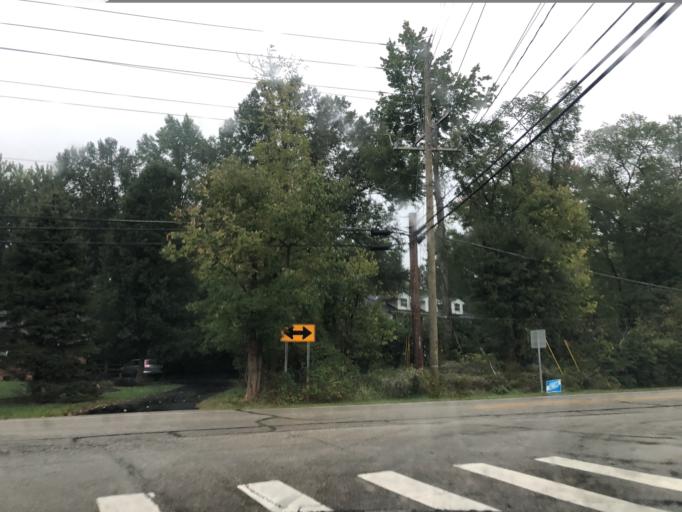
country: US
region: Ohio
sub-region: Hamilton County
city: The Village of Indian Hill
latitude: 39.2472
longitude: -84.3104
